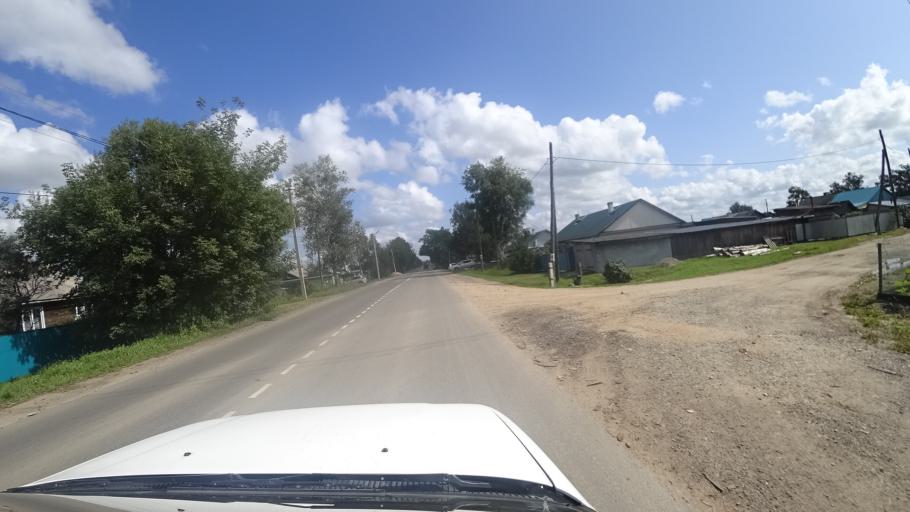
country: RU
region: Primorskiy
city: Dal'nerechensk
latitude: 45.9269
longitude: 133.7676
